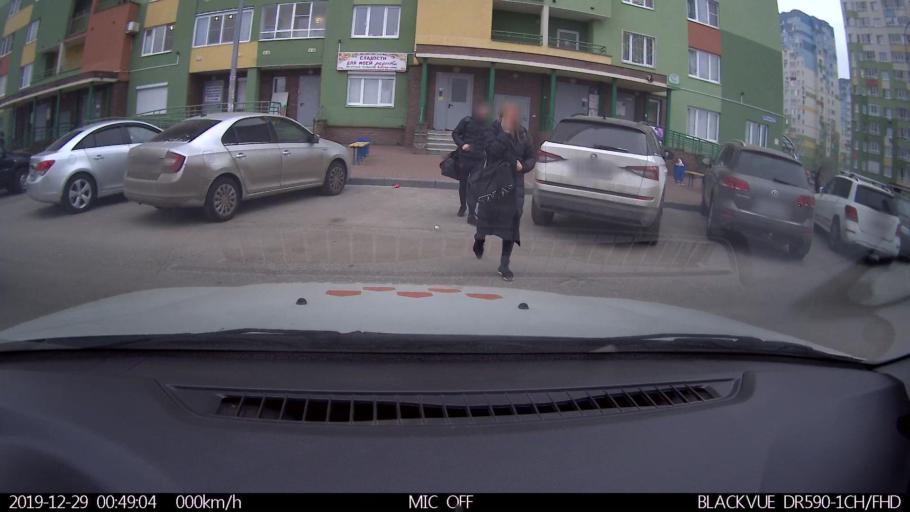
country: RU
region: Nizjnij Novgorod
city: Nizhniy Novgorod
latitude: 56.3415
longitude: 43.9531
